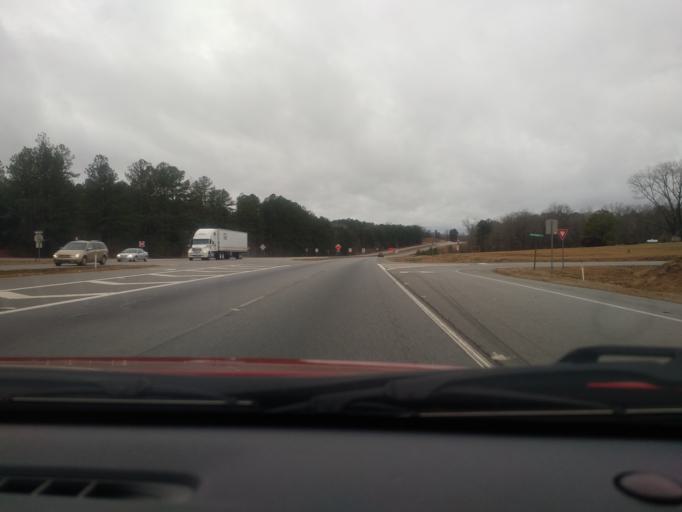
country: US
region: Georgia
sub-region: Henry County
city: Locust Grove
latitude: 33.2592
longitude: -84.1051
